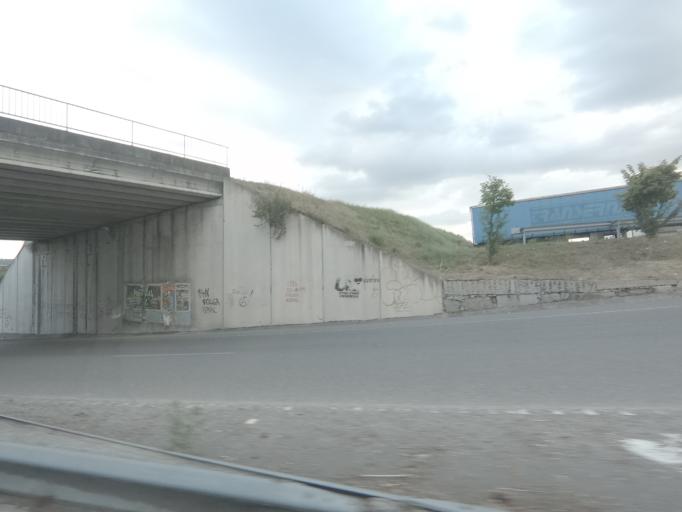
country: ES
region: Galicia
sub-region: Provincia de Ourense
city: Taboadela
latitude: 42.2874
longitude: -7.8278
